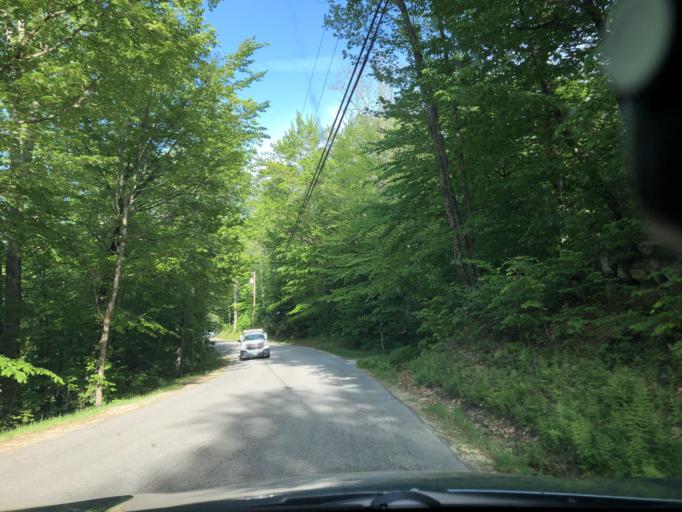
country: US
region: New Hampshire
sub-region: Merrimack County
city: New London
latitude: 43.4226
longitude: -71.9600
